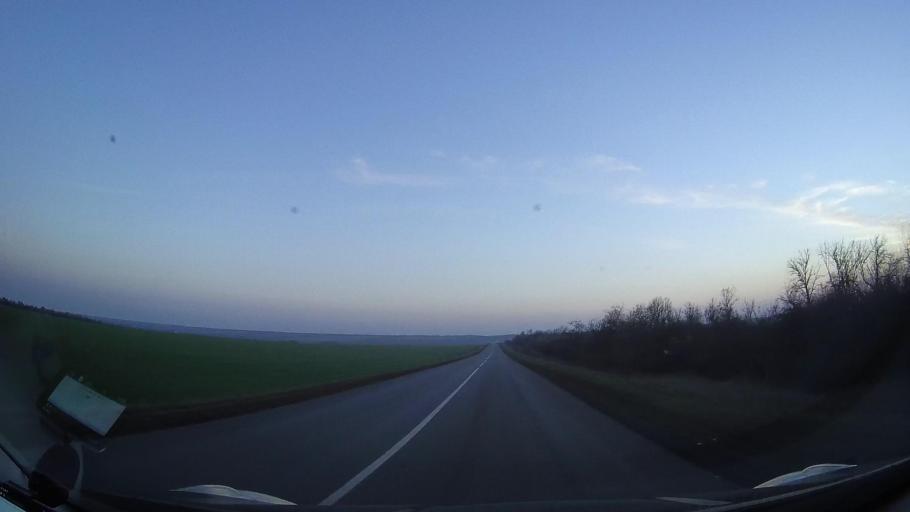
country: RU
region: Rostov
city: Zernograd
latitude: 46.9123
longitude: 40.3388
